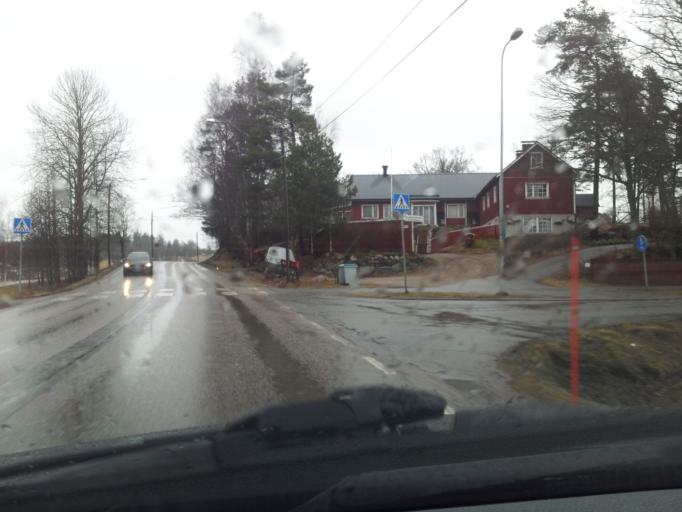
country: FI
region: Uusimaa
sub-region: Helsinki
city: Kirkkonummi
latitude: 60.1529
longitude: 24.5295
